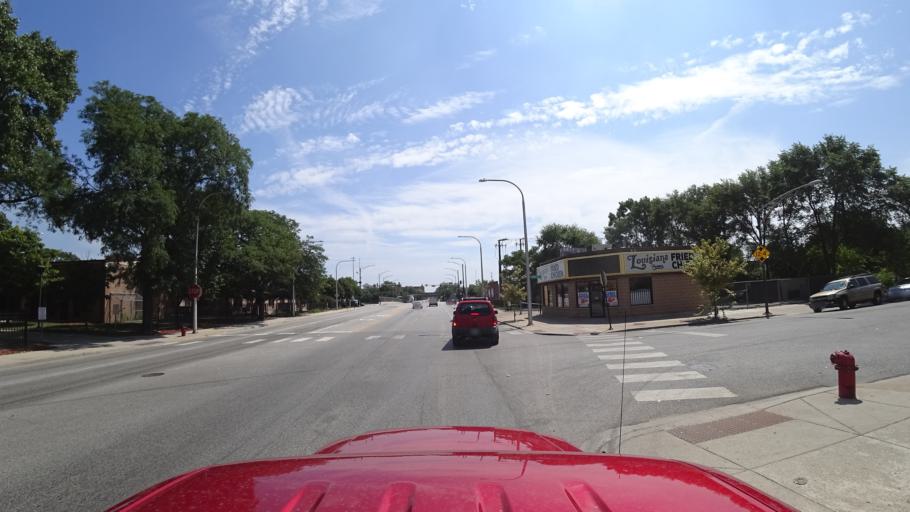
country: US
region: Illinois
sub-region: Cook County
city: Chicago
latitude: 41.8236
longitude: -87.6327
